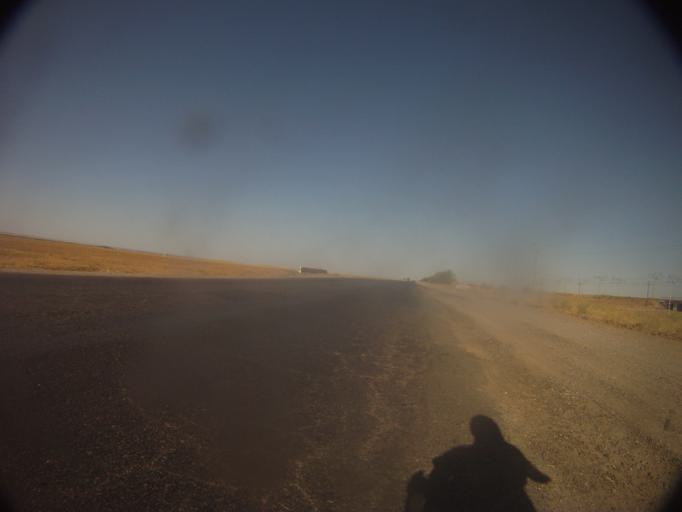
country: KZ
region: Zhambyl
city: Sarykemer
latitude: 42.9660
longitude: 71.5537
